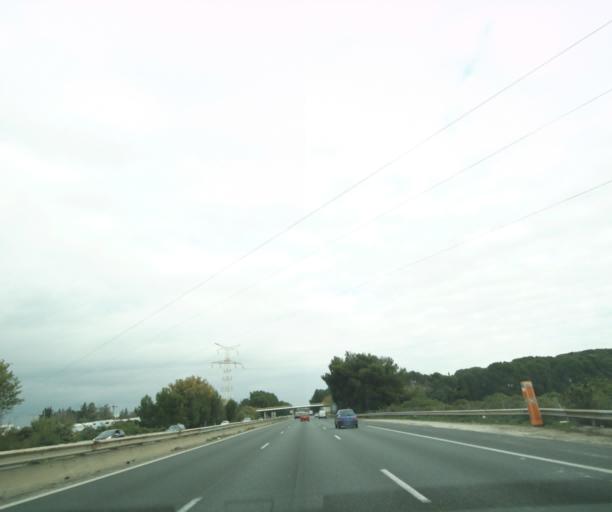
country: FR
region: Languedoc-Roussillon
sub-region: Departement de l'Herault
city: Lattes
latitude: 43.5960
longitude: 3.9099
